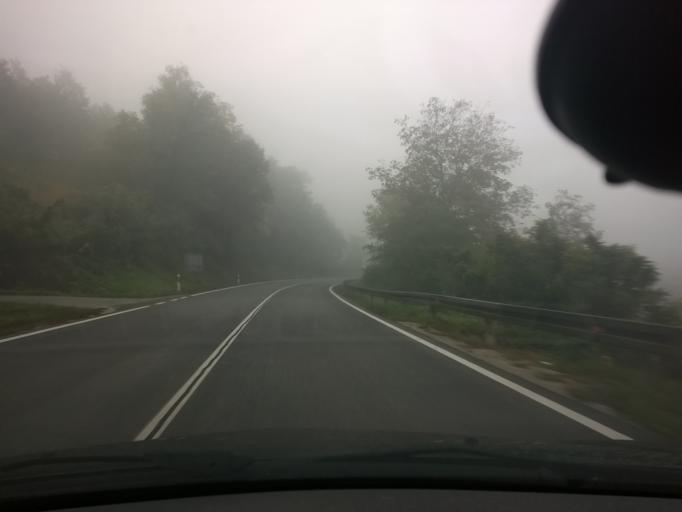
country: HR
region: Krapinsko-Zagorska
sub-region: Grad Krapina
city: Krapina
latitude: 46.1535
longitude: 15.8794
